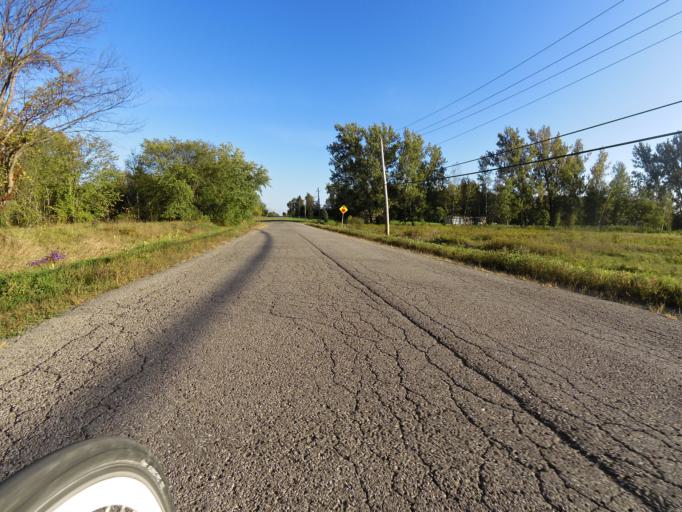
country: CA
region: Ontario
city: Bells Corners
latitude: 45.2158
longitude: -75.7129
